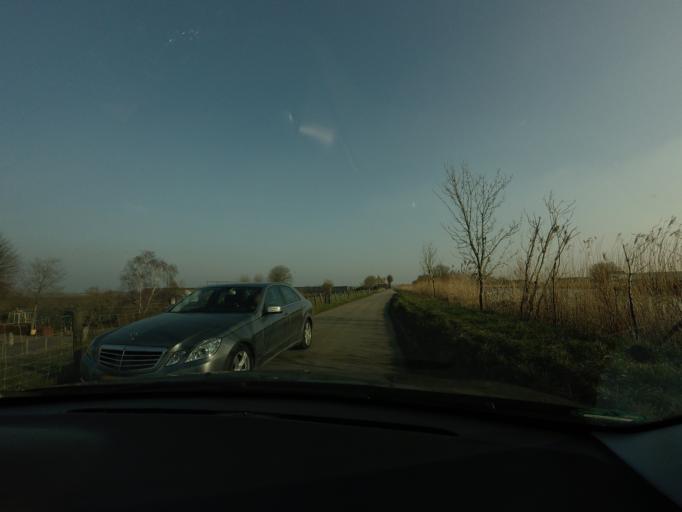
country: NL
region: South Holland
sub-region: Gemeente Kaag en Braassem
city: Leimuiden
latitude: 52.2208
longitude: 4.6940
